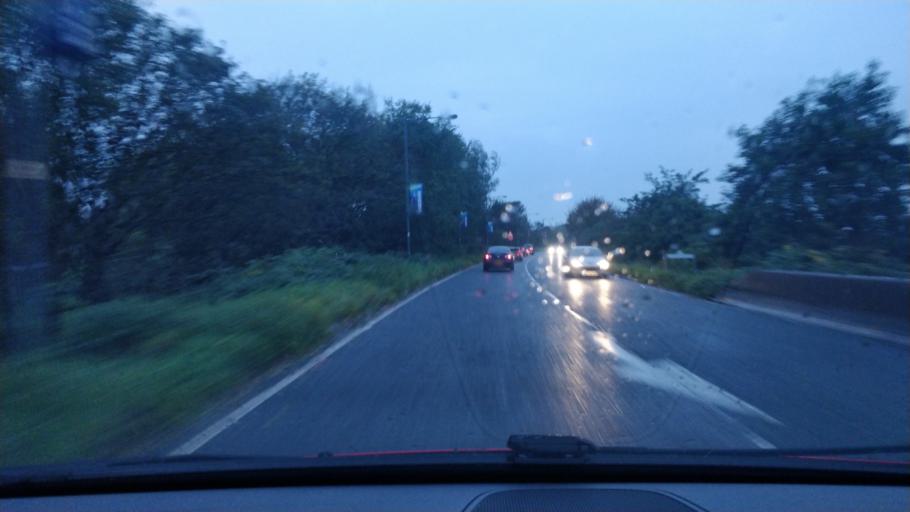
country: GB
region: England
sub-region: Blackpool
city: Blackpool
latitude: 53.7936
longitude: -3.0424
